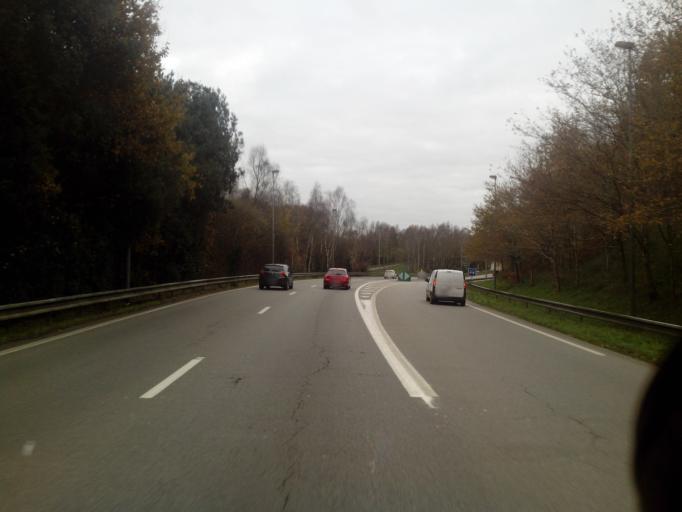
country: FR
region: Pays de la Loire
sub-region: Departement de la Loire-Atlantique
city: La Chapelle-sur-Erdre
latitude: 47.2627
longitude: -1.5578
